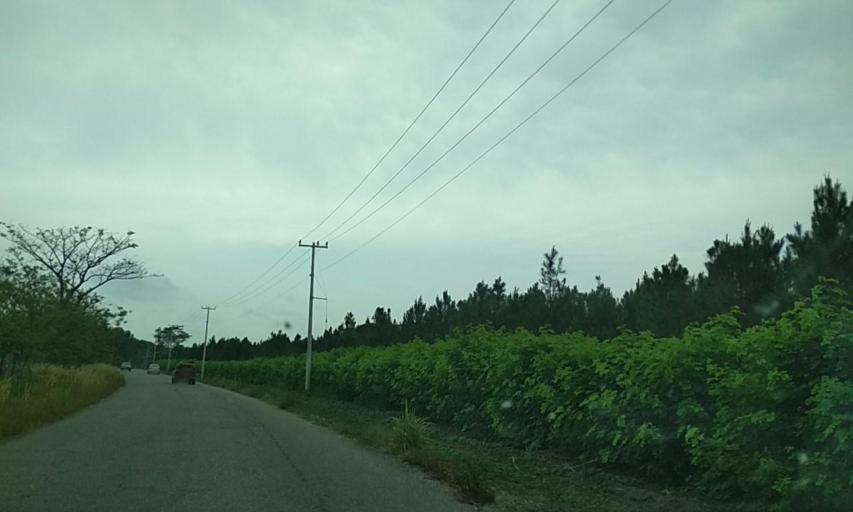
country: MX
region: Veracruz
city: Las Choapas
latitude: 17.8460
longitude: -94.1049
